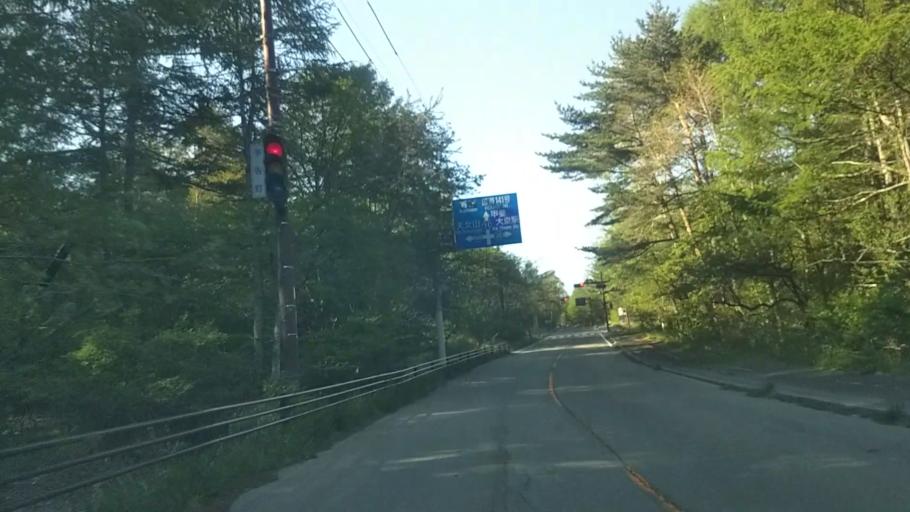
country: JP
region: Yamanashi
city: Nirasaki
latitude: 35.9153
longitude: 138.4040
